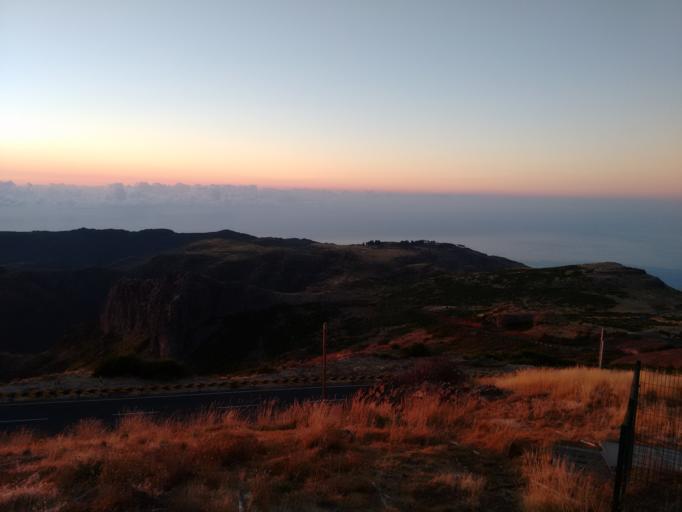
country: PT
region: Madeira
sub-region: Camara de Lobos
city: Curral das Freiras
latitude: 32.7352
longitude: -16.9284
